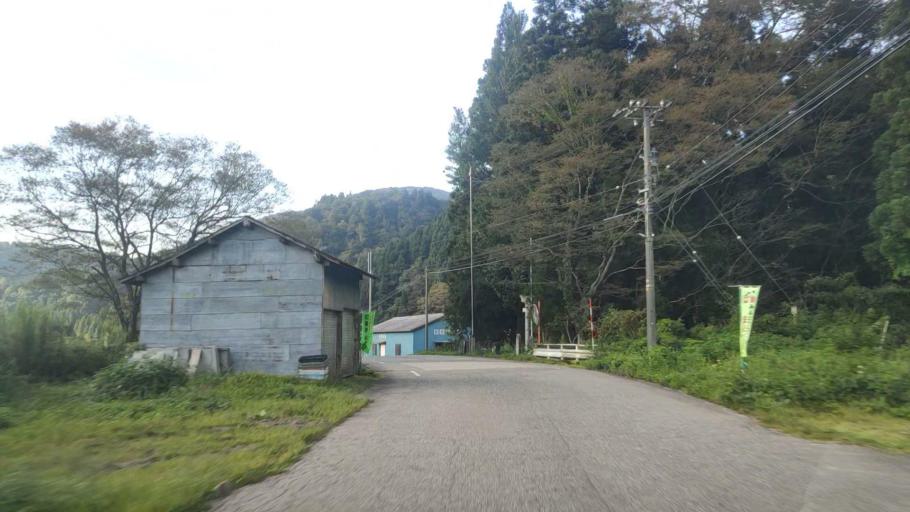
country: JP
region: Toyama
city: Yatsuomachi-higashikumisaka
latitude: 36.4755
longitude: 137.0853
